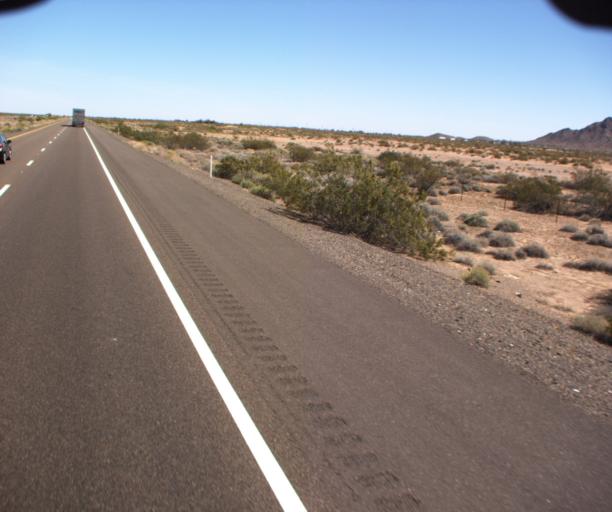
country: US
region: Arizona
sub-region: Yuma County
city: Wellton
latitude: 32.8083
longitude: -113.5200
